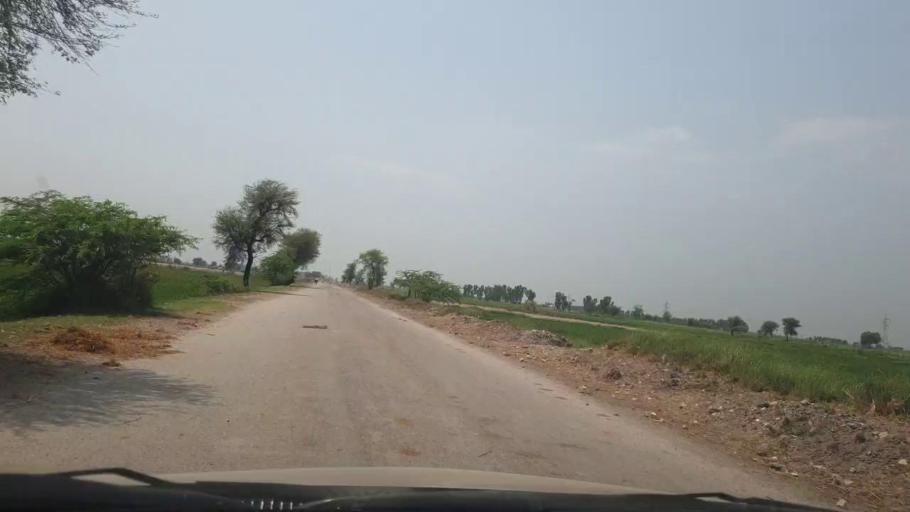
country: PK
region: Sindh
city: Ratodero
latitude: 27.7176
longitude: 68.2780
